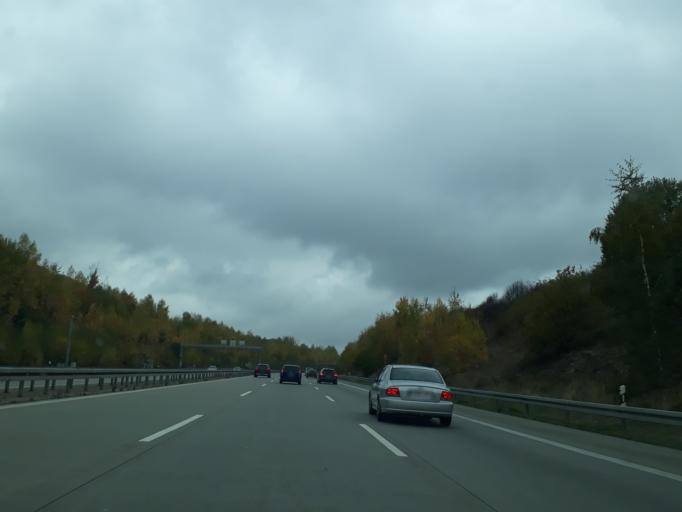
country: DE
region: Saxony
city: Freital
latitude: 51.0355
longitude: 13.6427
